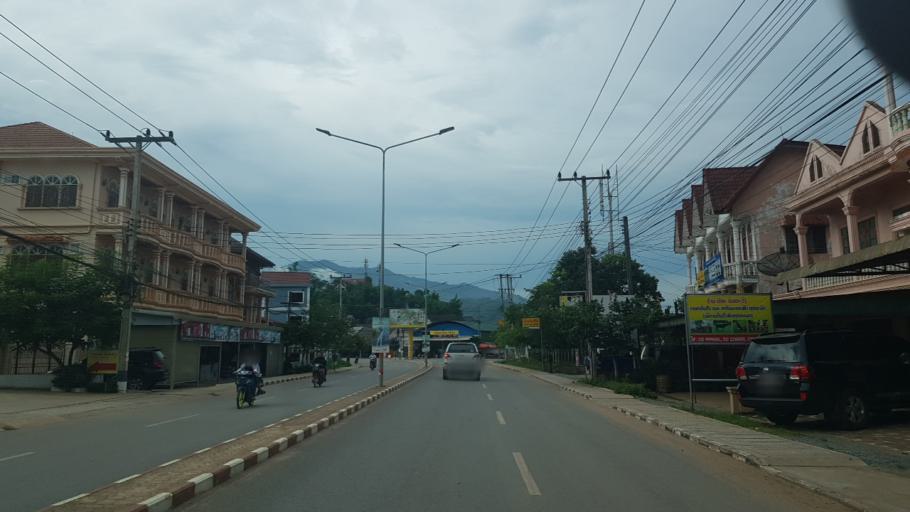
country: LA
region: Oudomxai
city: Muang Xay
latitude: 20.6844
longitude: 101.9874
